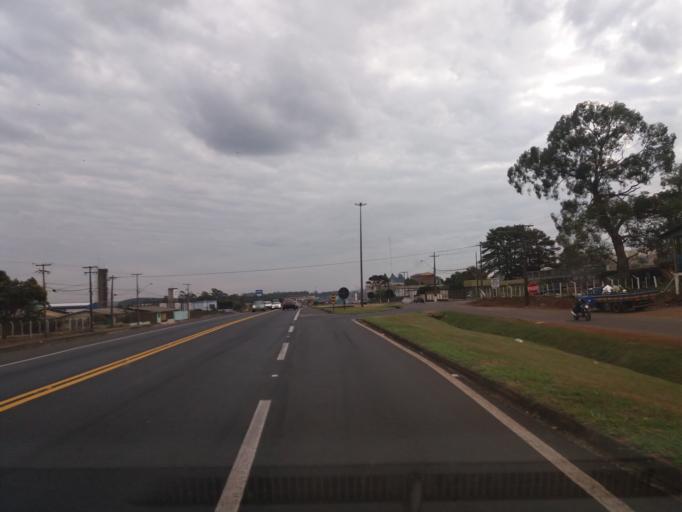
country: BR
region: Parana
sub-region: Cascavel
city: Cascavel
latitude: -24.9840
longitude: -53.4633
